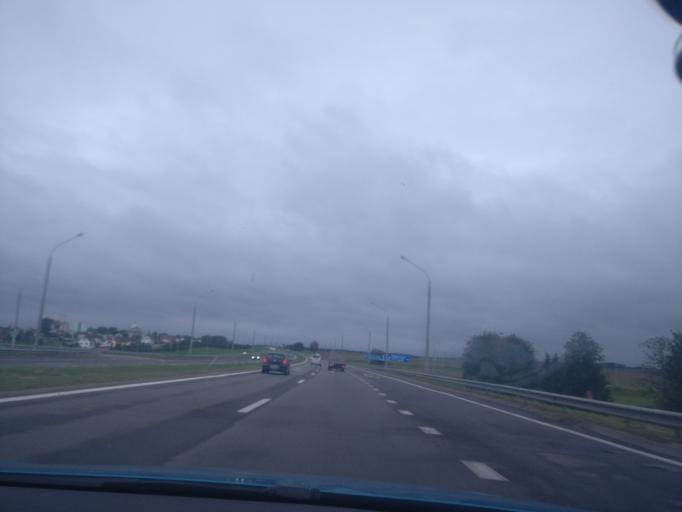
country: BY
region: Minsk
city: Slabada
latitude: 54.0159
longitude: 27.8905
